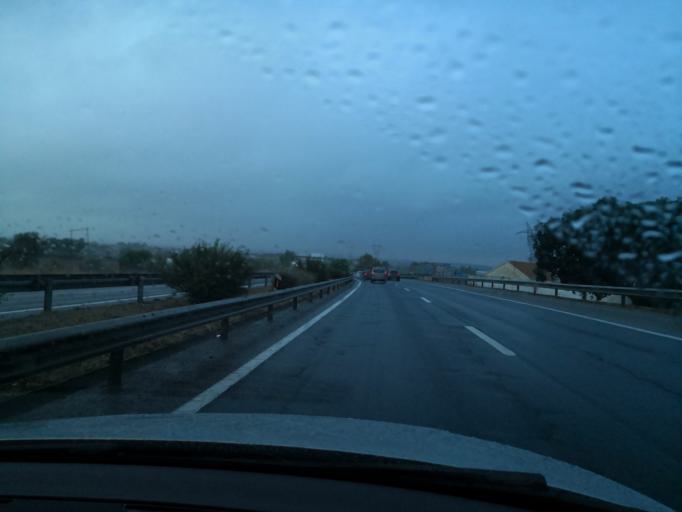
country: PT
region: Setubal
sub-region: Moita
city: Moita
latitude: 38.6514
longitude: -8.9680
